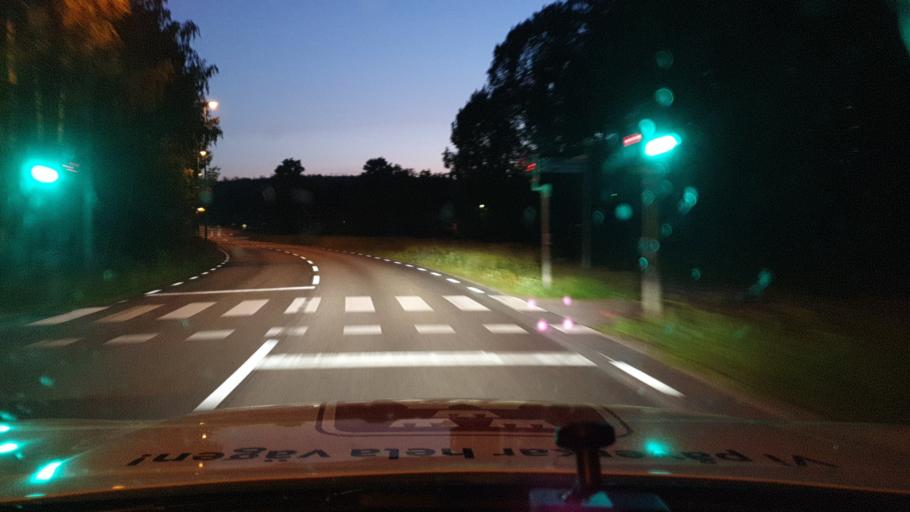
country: SE
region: OErebro
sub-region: Karlskoga Kommun
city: Karlskoga
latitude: 59.3483
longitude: 14.5781
